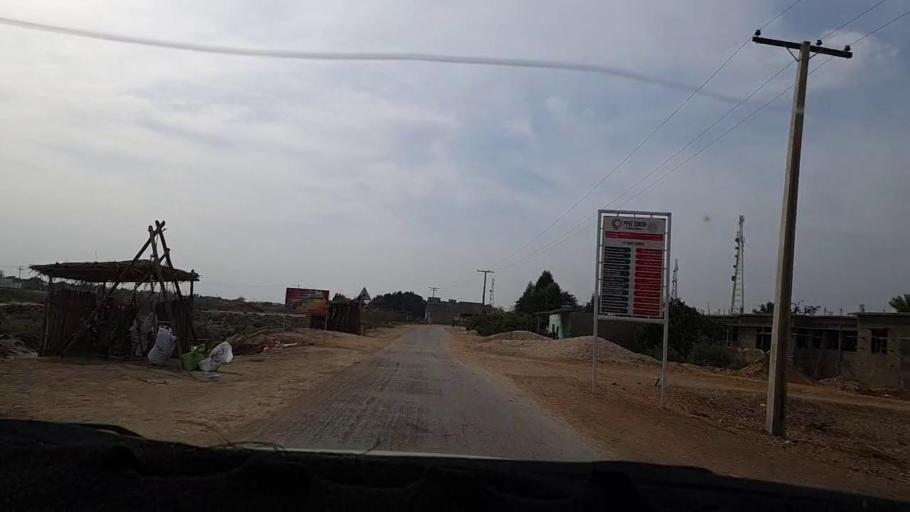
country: PK
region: Sindh
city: Pithoro
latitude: 25.5183
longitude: 69.2385
